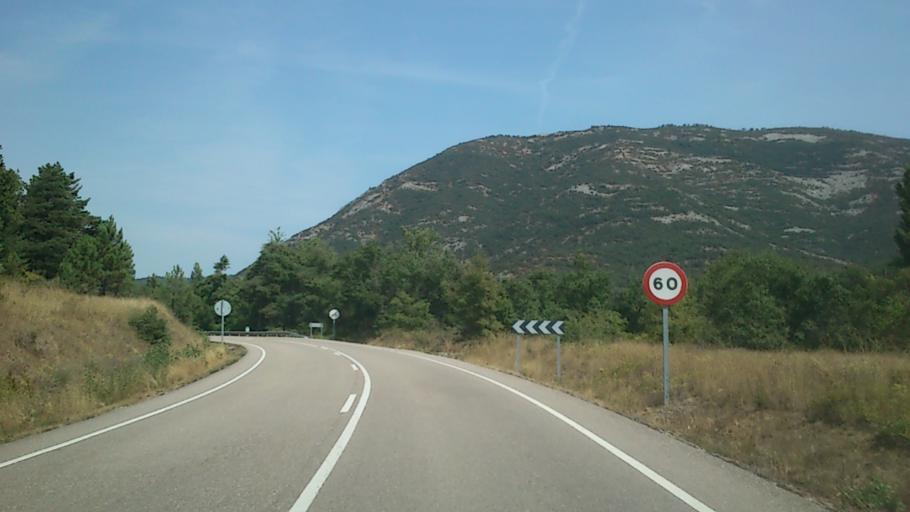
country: ES
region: Castille and Leon
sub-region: Provincia de Burgos
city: Trespaderne
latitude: 42.8790
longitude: -3.3263
